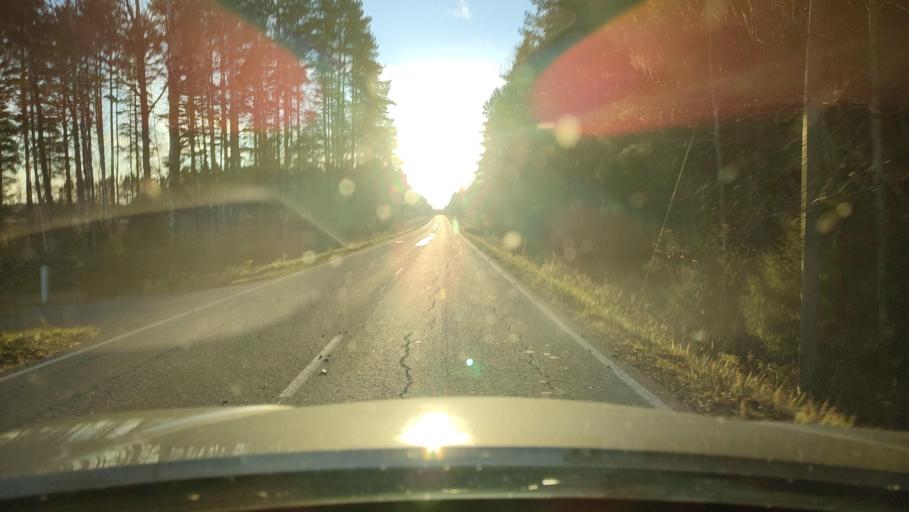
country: FI
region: Ostrobothnia
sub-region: Vaasa
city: Malax
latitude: 62.6984
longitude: 21.5764
